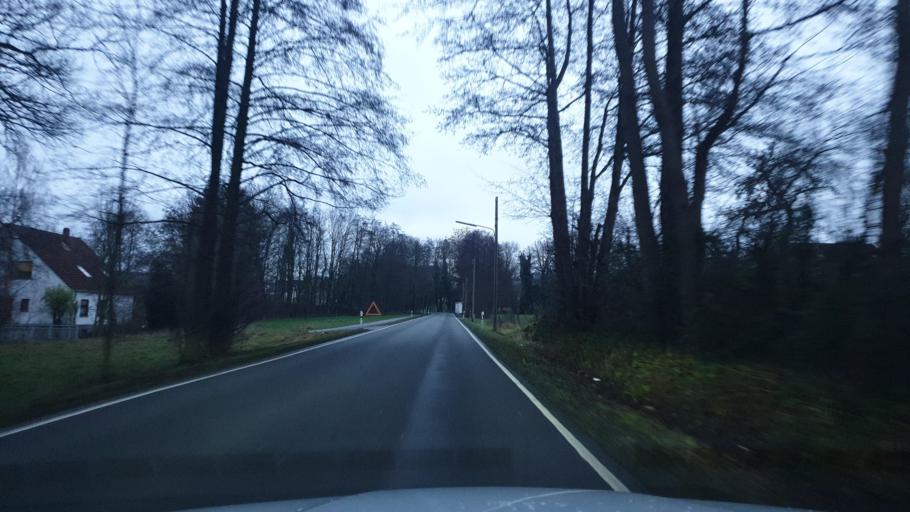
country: DE
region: North Rhine-Westphalia
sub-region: Regierungsbezirk Detmold
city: Vlotho
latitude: 52.1669
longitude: 8.8256
